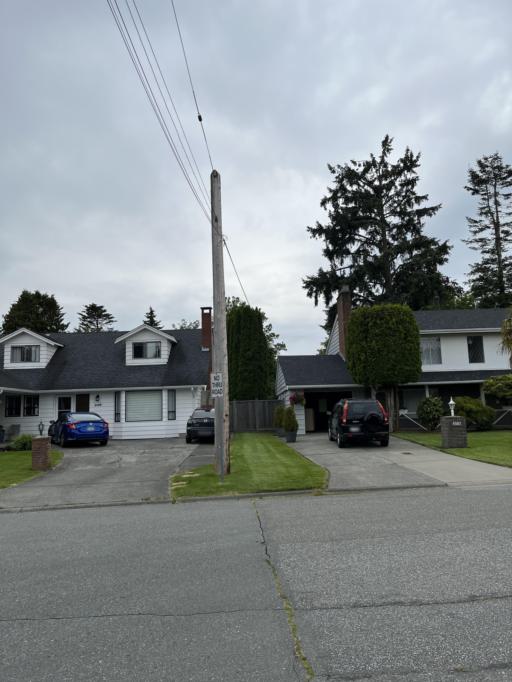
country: CA
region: British Columbia
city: Ladner
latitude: 49.0854
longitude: -123.0772
